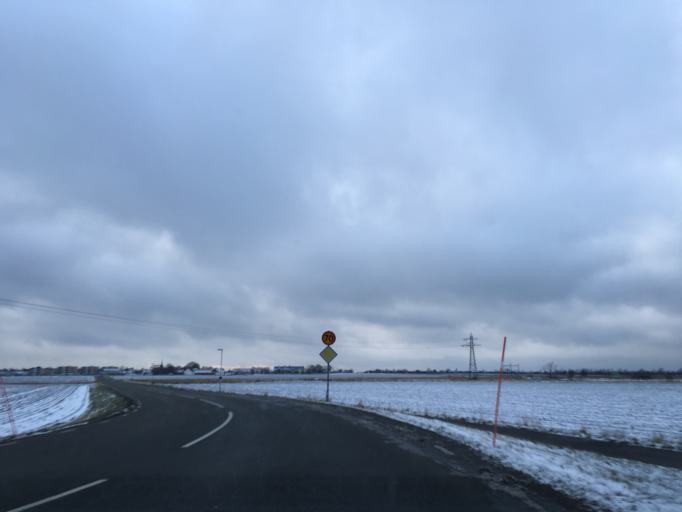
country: SE
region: Skane
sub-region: Vellinge Kommun
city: Hollviken
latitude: 55.4319
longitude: 12.9836
